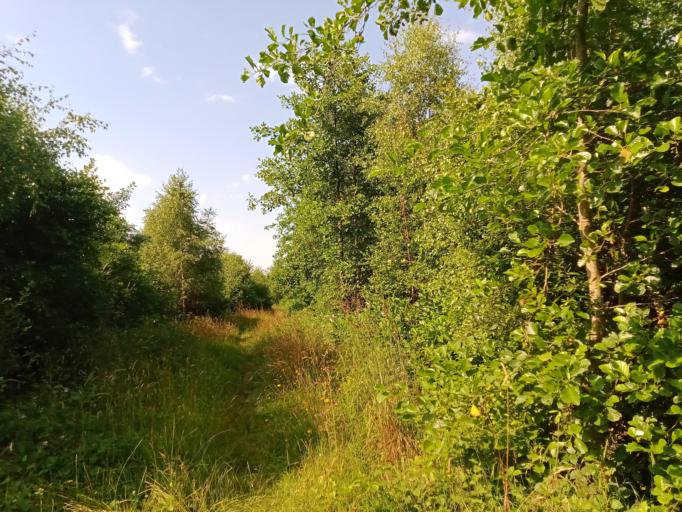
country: IE
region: Leinster
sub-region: Laois
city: Abbeyleix
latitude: 52.9038
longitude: -7.3565
